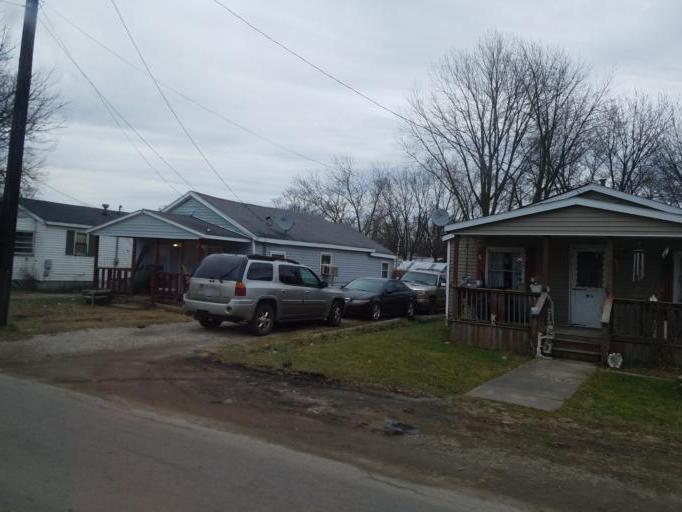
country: US
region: Ohio
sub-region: Marion County
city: Marion
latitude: 40.5957
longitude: -83.1132
